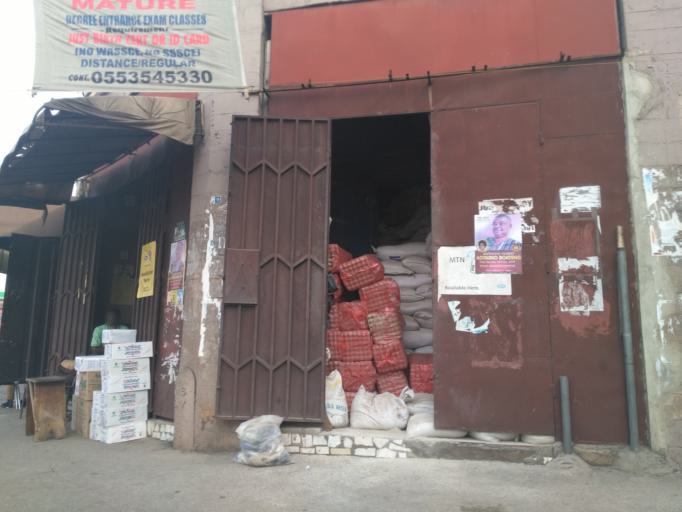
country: GH
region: Ashanti
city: Kumasi
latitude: 6.6892
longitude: -1.6131
